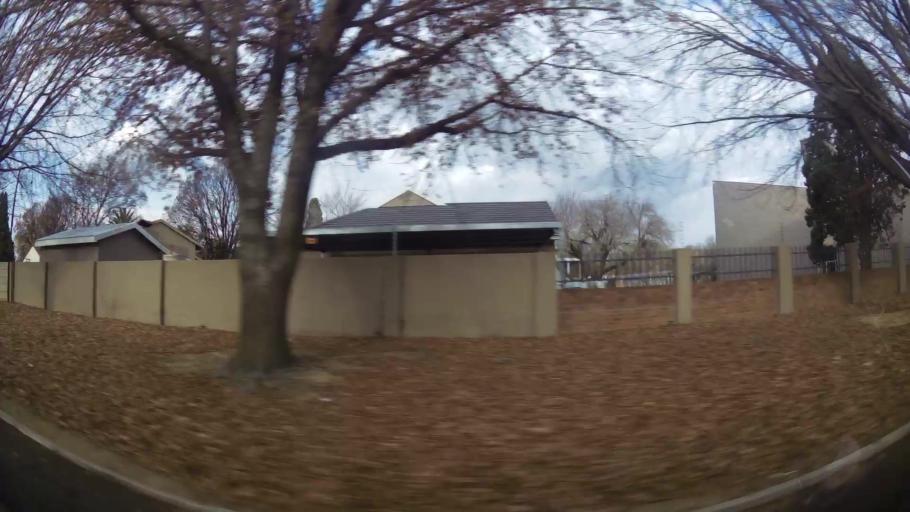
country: ZA
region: Orange Free State
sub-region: Fezile Dabi District Municipality
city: Sasolburg
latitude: -26.8018
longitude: 27.8181
